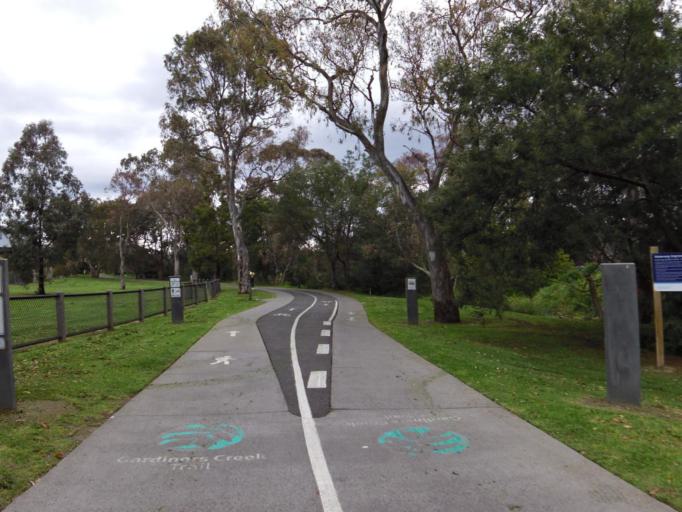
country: AU
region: Victoria
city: Carnegie
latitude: -37.8726
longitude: 145.0690
